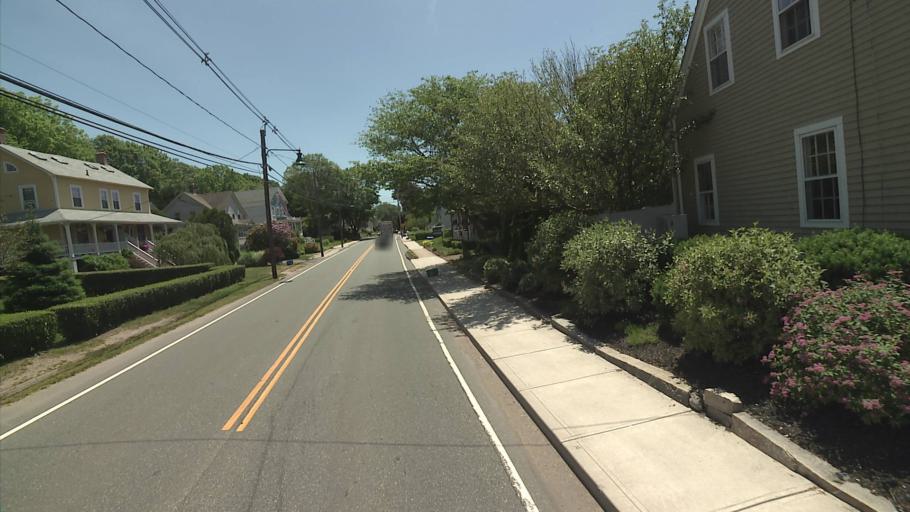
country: US
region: Connecticut
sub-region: New London County
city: Mystic
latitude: 41.3542
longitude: -71.9617
